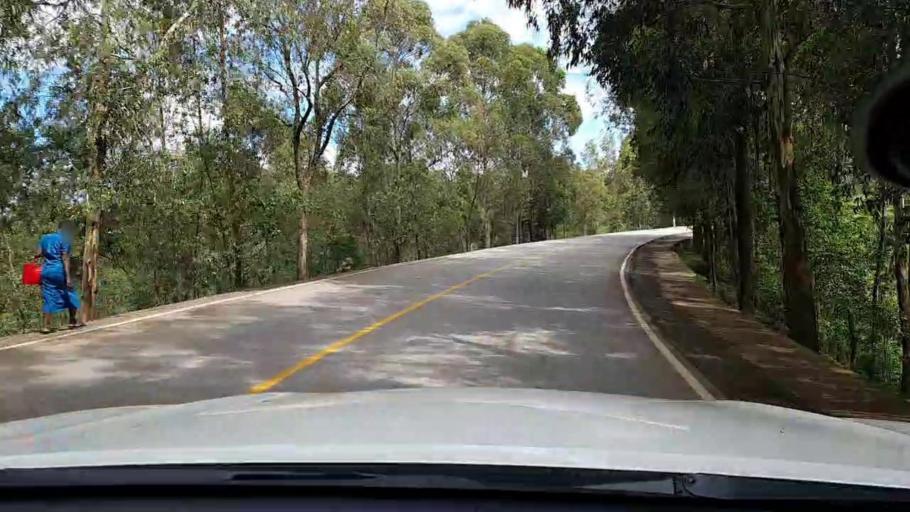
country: RW
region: Kigali
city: Kigali
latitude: -1.8194
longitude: 29.9408
